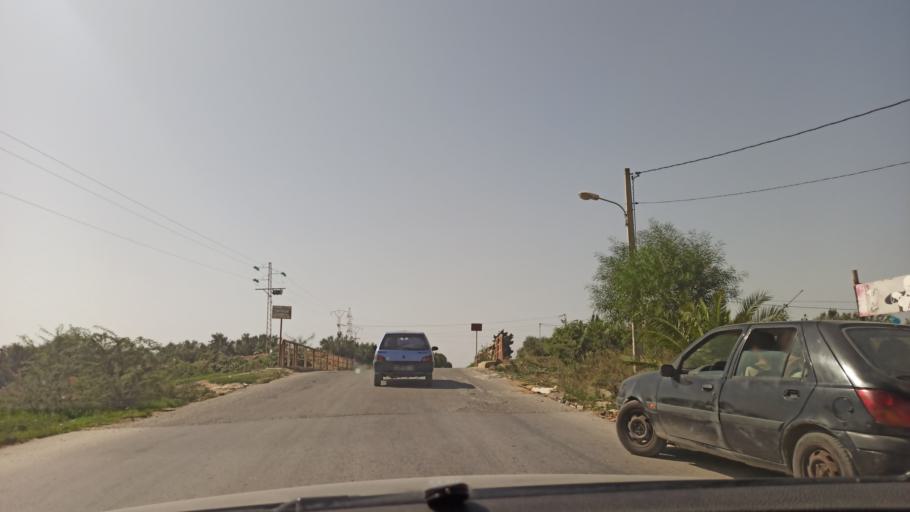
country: TN
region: Manouba
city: Manouba
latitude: 36.7499
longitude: 10.0995
